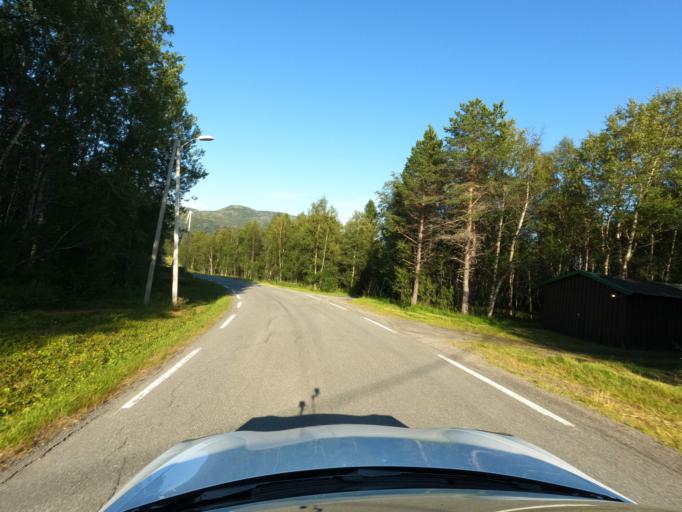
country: NO
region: Nordland
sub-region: Narvik
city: Bjerkvik
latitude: 68.4765
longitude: 17.5229
